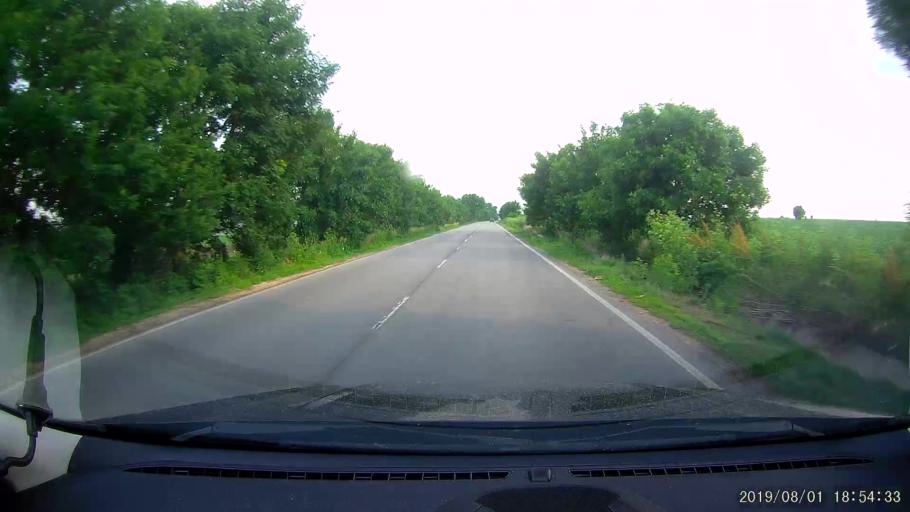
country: BG
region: Shumen
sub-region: Obshtina Shumen
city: Shumen
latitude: 43.1959
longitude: 27.0023
